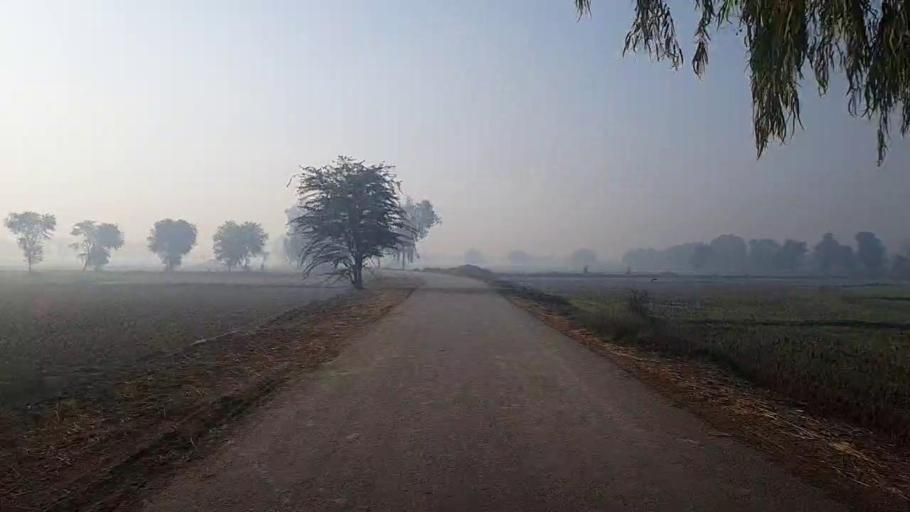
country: PK
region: Sindh
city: Mehar
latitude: 27.1443
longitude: 67.8227
